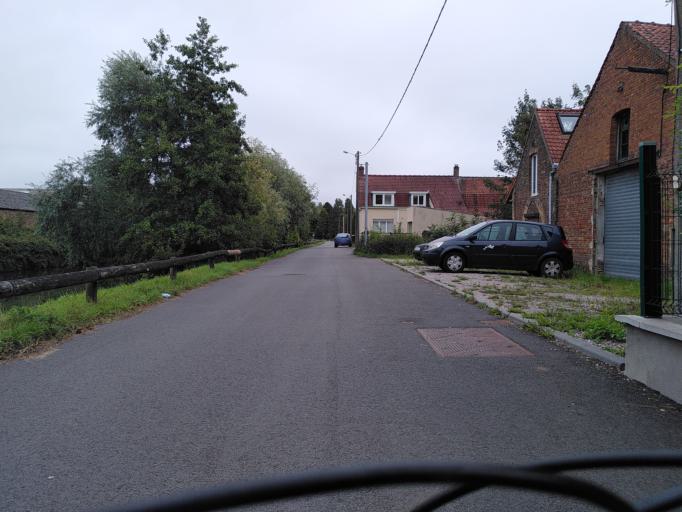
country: FR
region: Nord-Pas-de-Calais
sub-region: Departement du Nord
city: Merville
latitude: 50.6373
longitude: 2.6320
